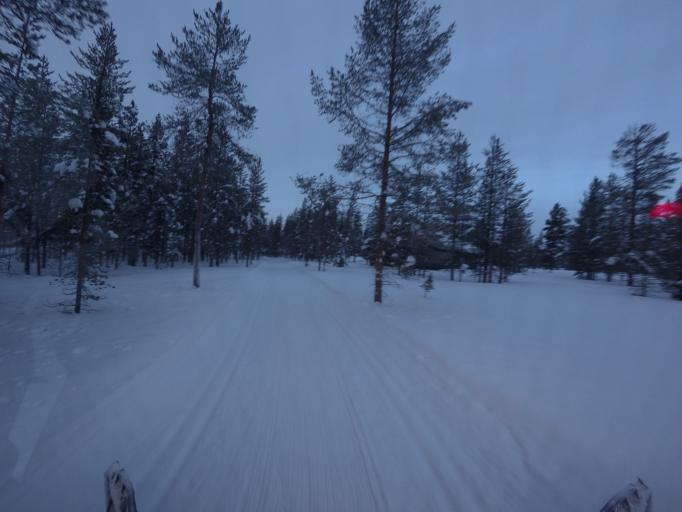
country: FI
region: Lapland
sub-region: Tunturi-Lappi
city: Kolari
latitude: 67.6239
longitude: 24.1582
